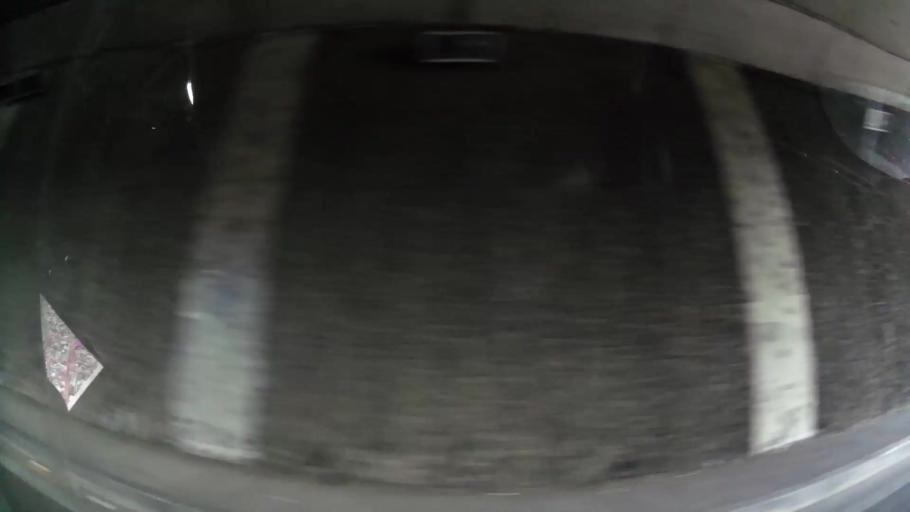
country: MQ
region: Martinique
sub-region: Martinique
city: Fort-de-France
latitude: 14.6090
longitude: -61.0670
